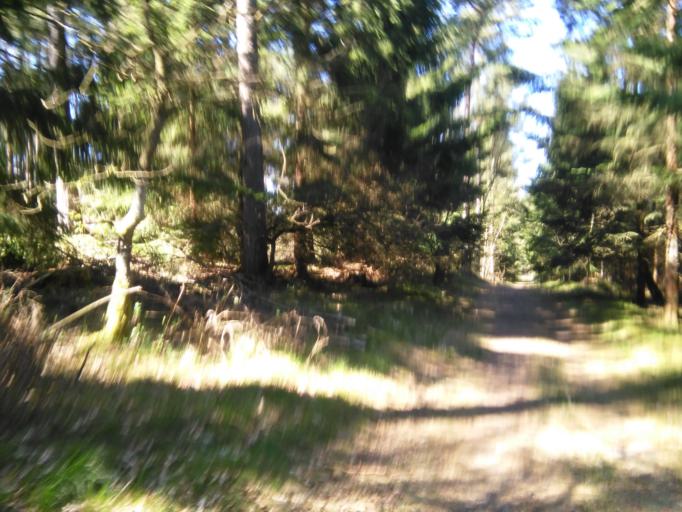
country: DK
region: Central Jutland
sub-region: Odder Kommune
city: Odder
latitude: 55.8868
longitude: 10.0860
